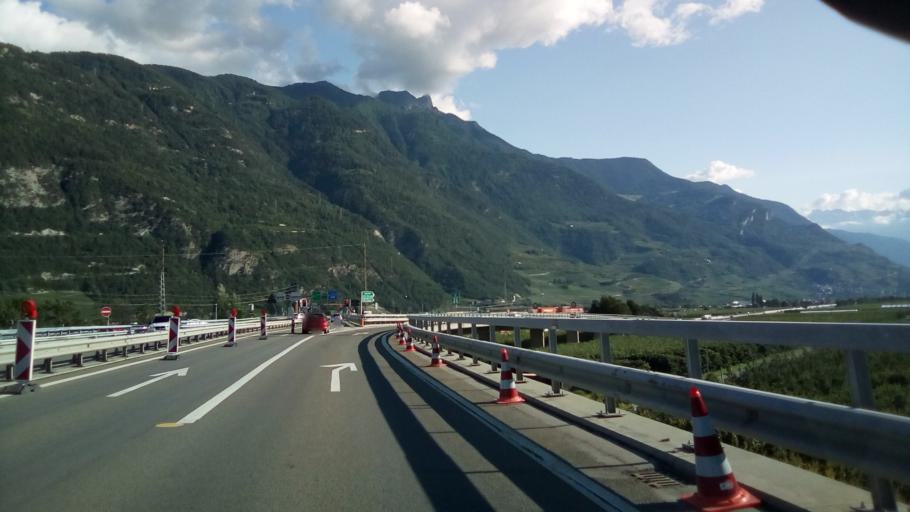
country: CH
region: Valais
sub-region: Martigny District
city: Riddes
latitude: 46.1745
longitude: 7.2144
